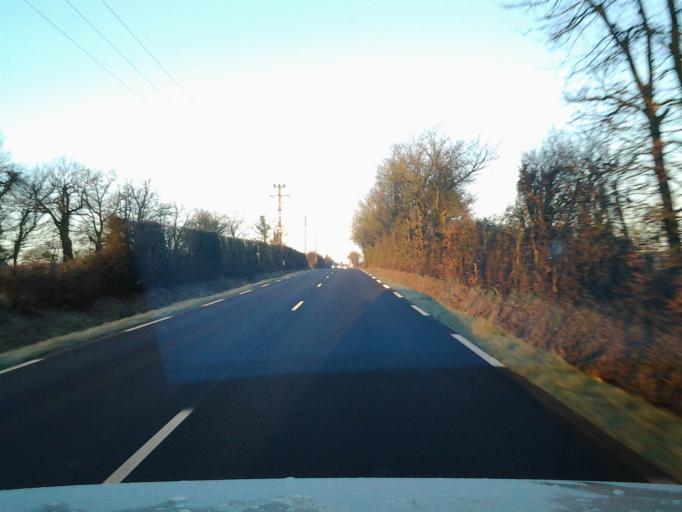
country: FR
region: Pays de la Loire
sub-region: Departement de la Vendee
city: Les Landes-Genusson
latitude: 46.9583
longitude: -1.1037
